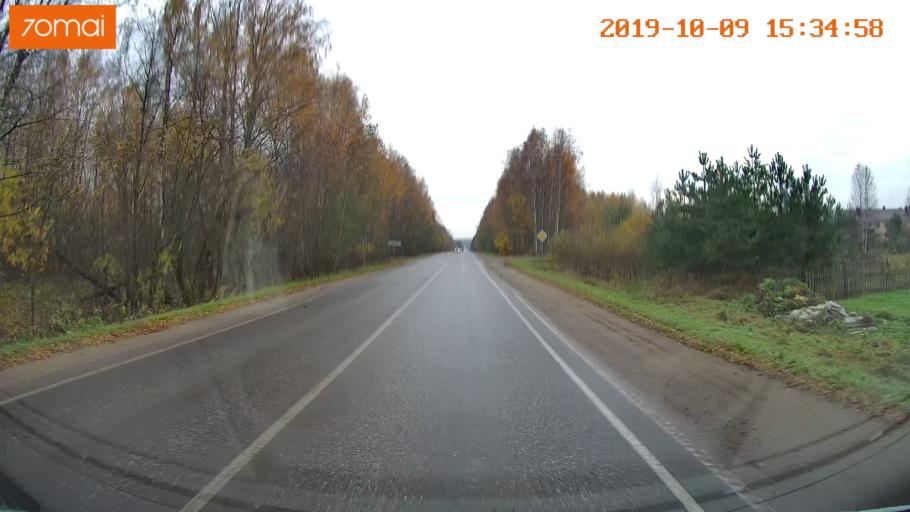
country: RU
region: Kostroma
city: Oktyabr'skiy
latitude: 57.9366
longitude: 41.2363
